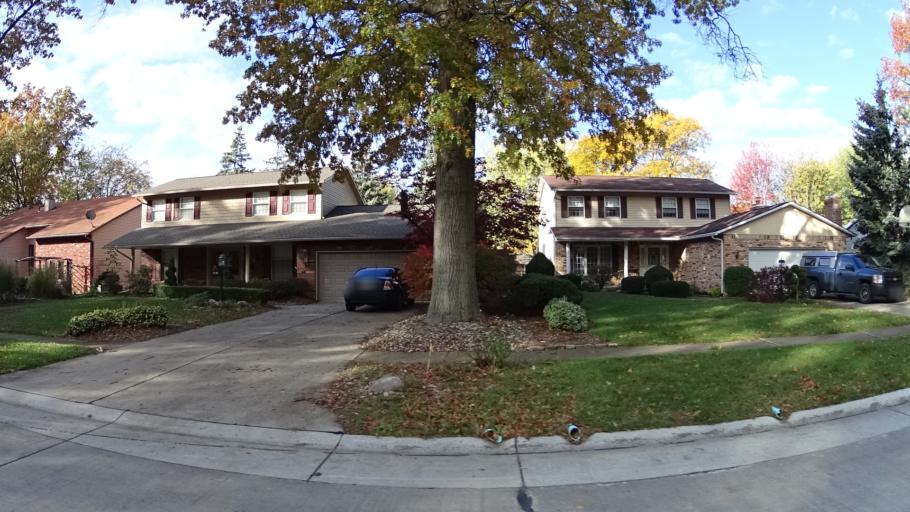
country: US
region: Ohio
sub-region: Lorain County
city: Lorain
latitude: 41.4313
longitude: -82.1810
